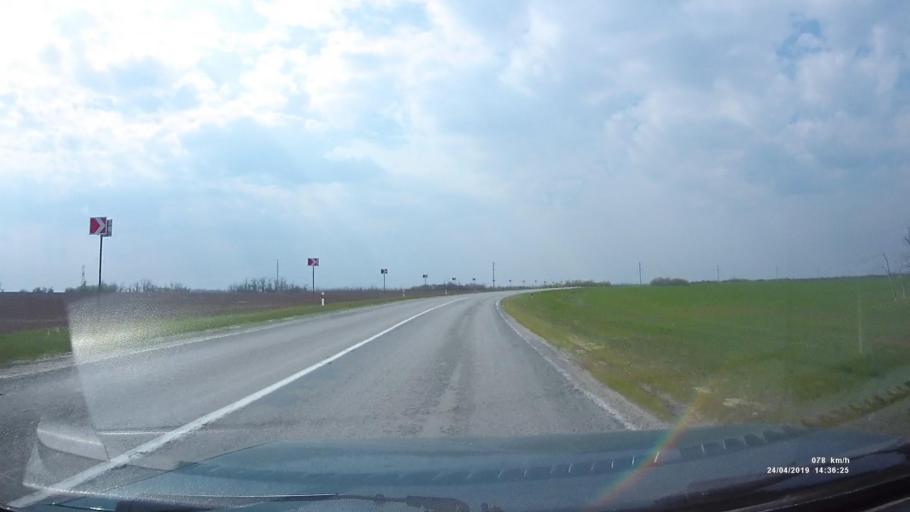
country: RU
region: Rostov
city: Remontnoye
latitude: 46.3755
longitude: 43.8919
